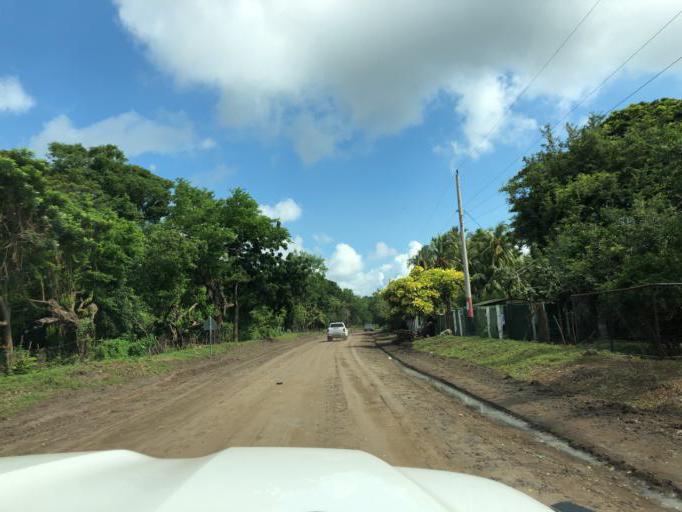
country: NI
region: Granada
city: Granada
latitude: 11.9939
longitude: -85.9376
